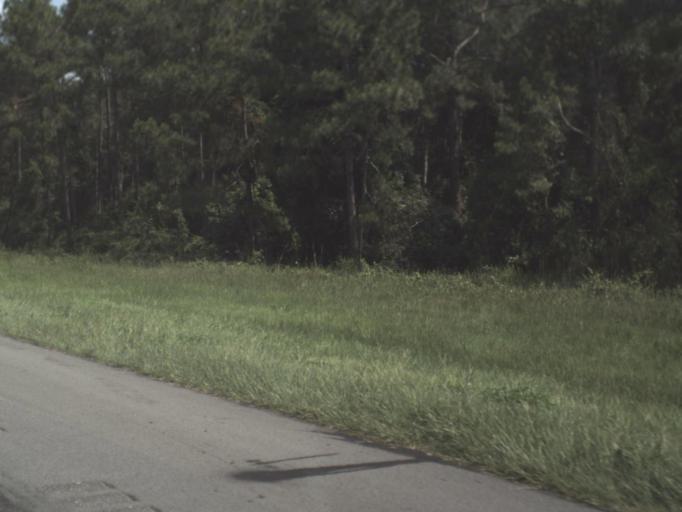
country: US
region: Georgia
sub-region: Echols County
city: Statenville
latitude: 30.6017
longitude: -83.1268
